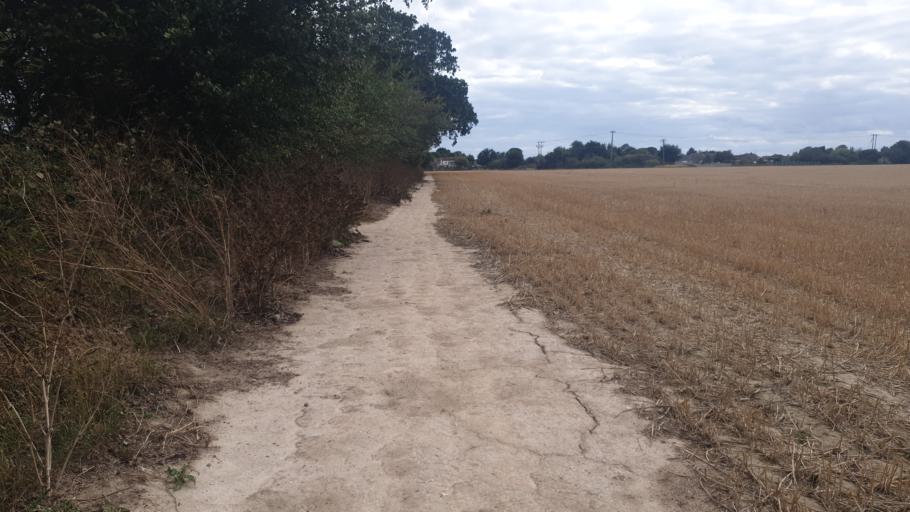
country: GB
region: England
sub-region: Essex
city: Frinton-on-Sea
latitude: 51.8472
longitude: 1.2355
